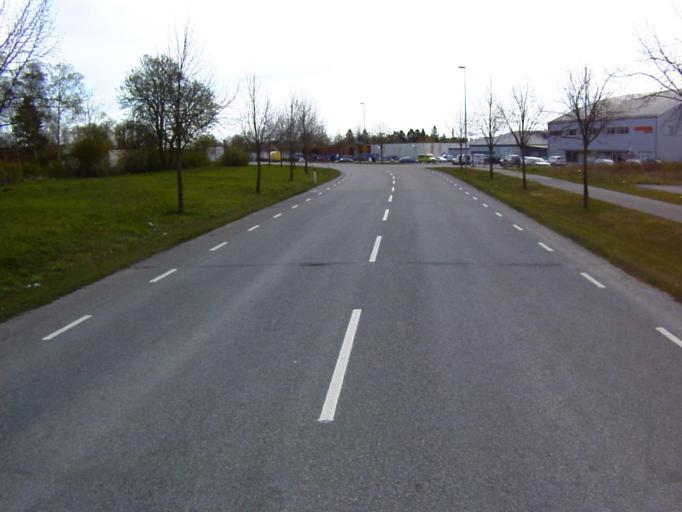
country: SE
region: Skane
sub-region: Kristianstads Kommun
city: Kristianstad
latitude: 56.0449
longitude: 14.1447
